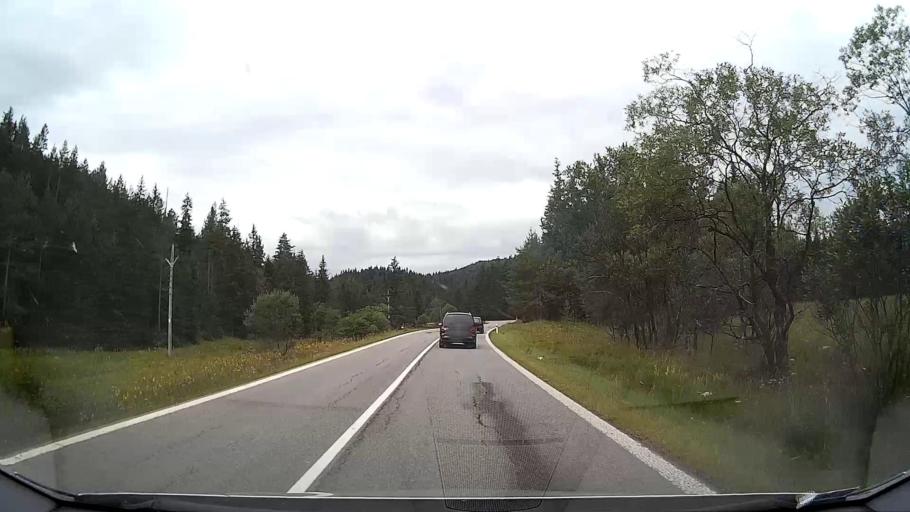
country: SK
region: Kosicky
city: Dobsina
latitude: 48.8788
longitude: 20.2307
